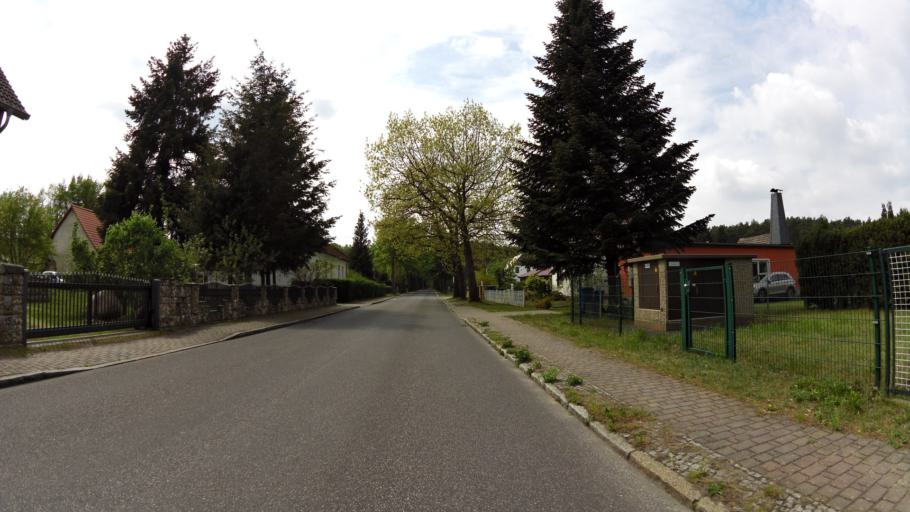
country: DE
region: Brandenburg
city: Bestensee
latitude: 52.2545
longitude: 13.7288
